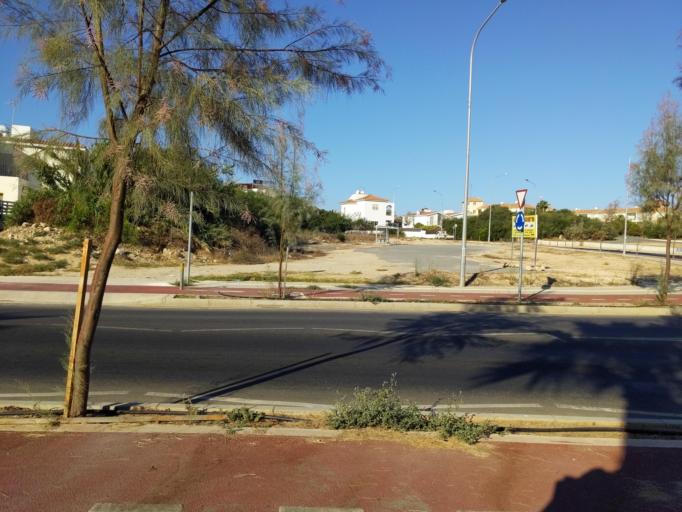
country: CY
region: Ammochostos
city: Protaras
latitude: 35.0259
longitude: 34.0402
